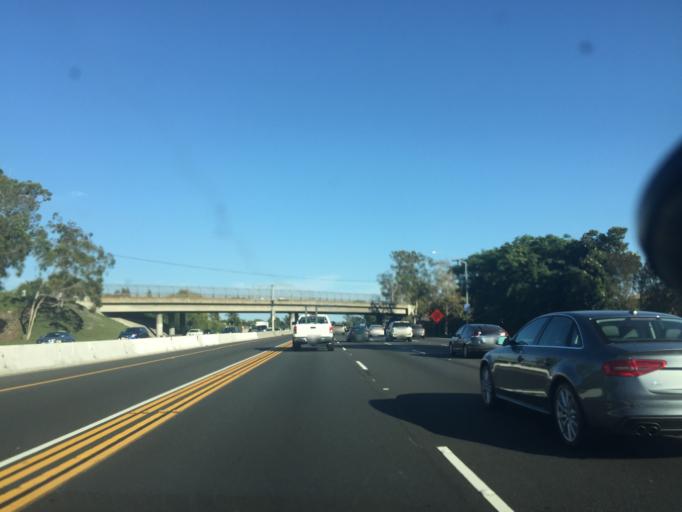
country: US
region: California
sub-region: Orange County
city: Fountain Valley
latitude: 33.7137
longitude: -117.9645
